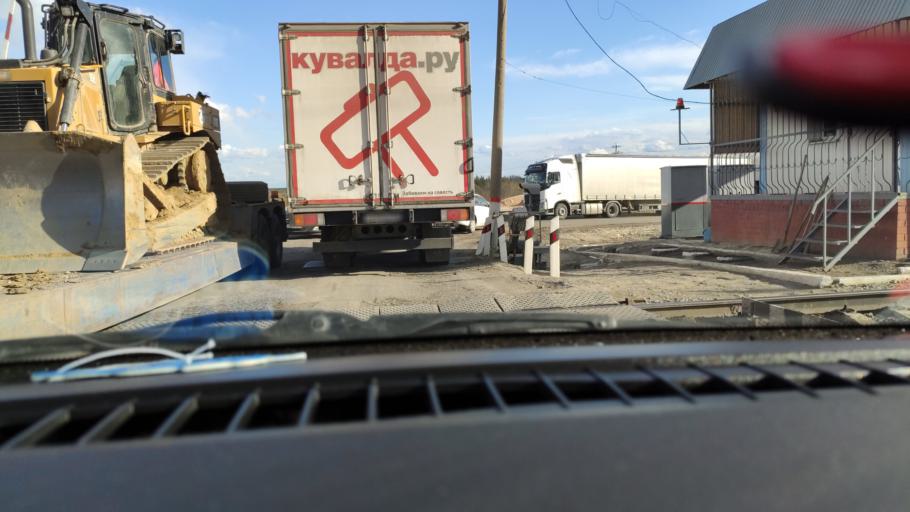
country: RU
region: Saratov
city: Sinodskoye
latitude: 52.0092
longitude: 46.6867
